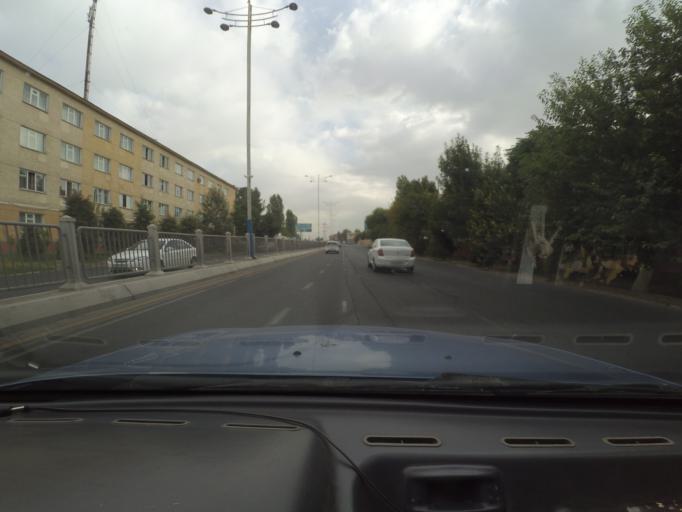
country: UZ
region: Toshkent
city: Salor
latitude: 41.3638
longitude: 69.3932
